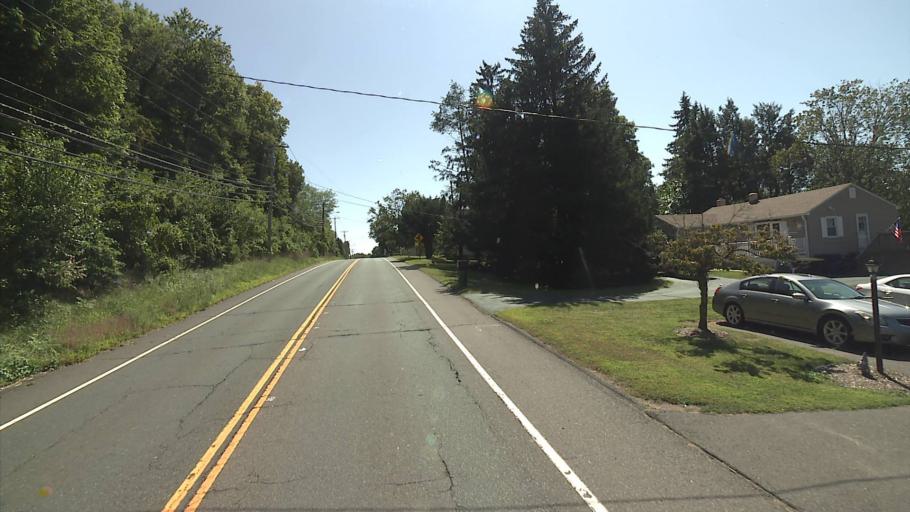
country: US
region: Connecticut
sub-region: Hartford County
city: Thompsonville
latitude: 41.9919
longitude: -72.6137
